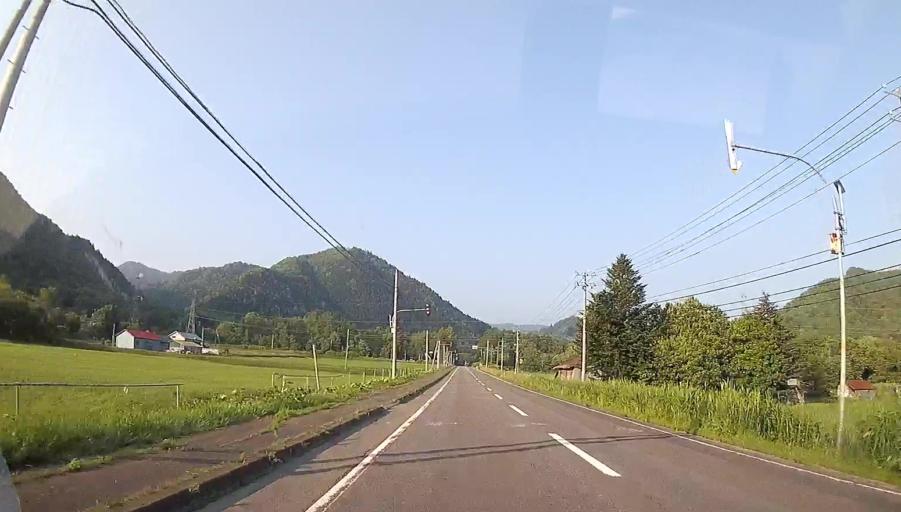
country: JP
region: Hokkaido
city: Shimo-furano
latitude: 42.8894
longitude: 142.4658
